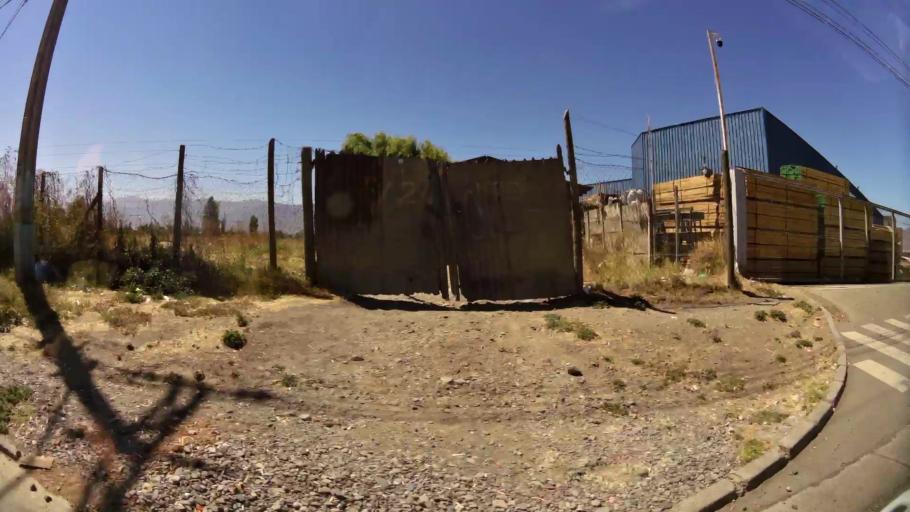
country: CL
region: O'Higgins
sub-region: Provincia de Cachapoal
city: Rancagua
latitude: -34.1542
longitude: -70.7268
